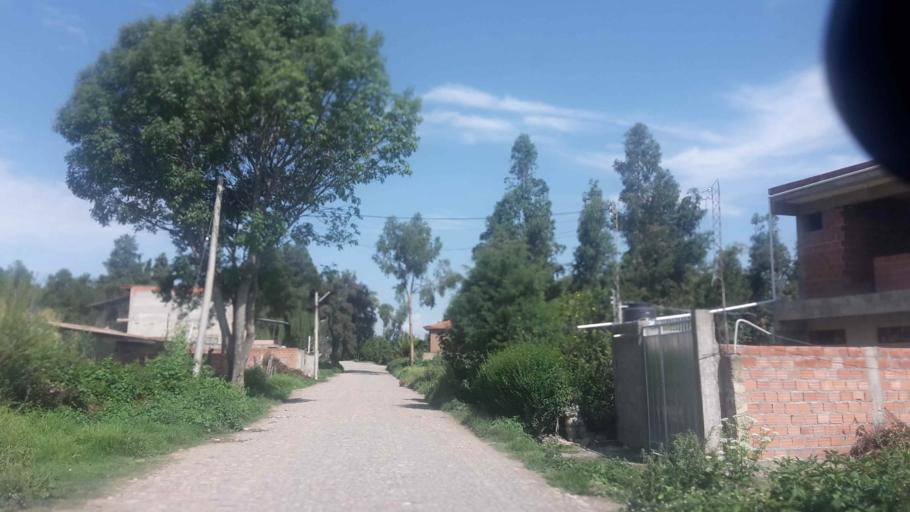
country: BO
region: Cochabamba
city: Cochabamba
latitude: -17.3632
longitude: -66.2093
